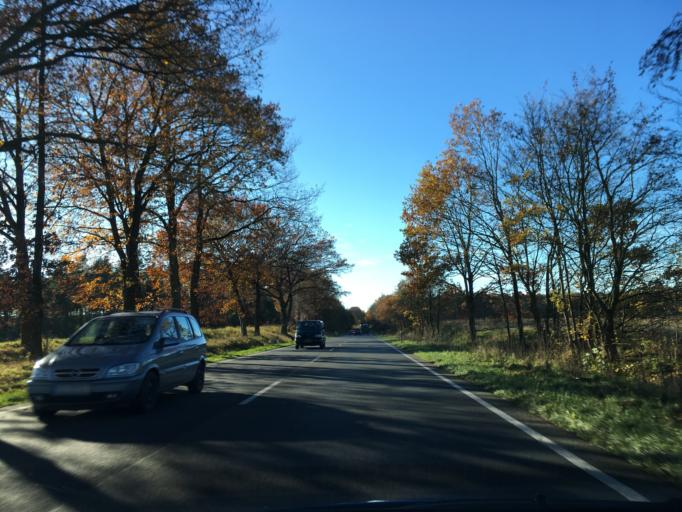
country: DE
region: Lower Saxony
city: Betzendorf
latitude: 53.1455
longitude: 10.2772
